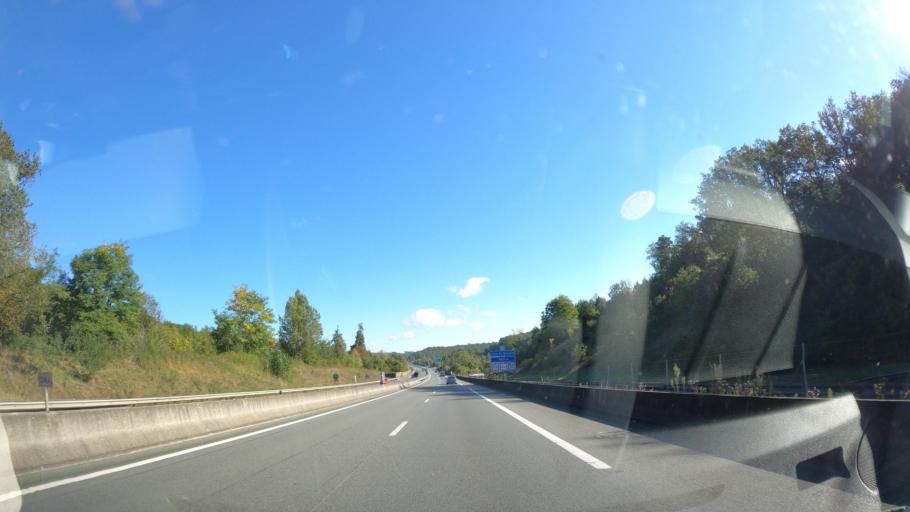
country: FR
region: Aquitaine
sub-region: Departement de la Dordogne
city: Atur
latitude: 45.1444
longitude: 0.7958
